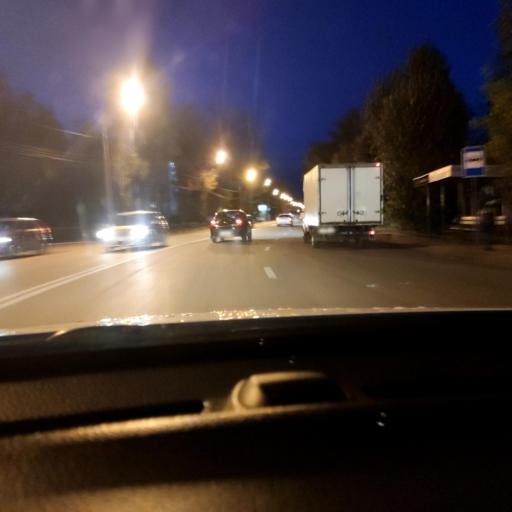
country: RU
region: Voronezj
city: Voronezh
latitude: 51.6476
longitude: 39.2675
